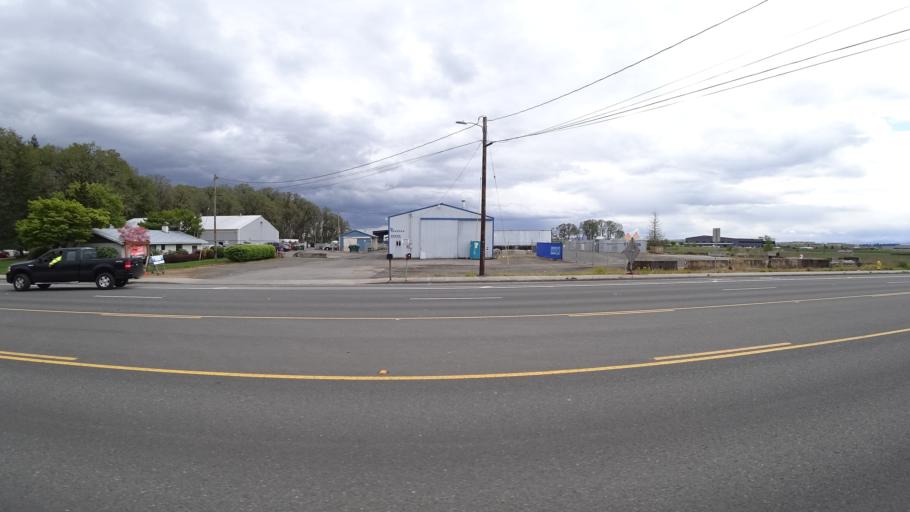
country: US
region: Oregon
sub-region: Washington County
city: Hillsboro
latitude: 45.5511
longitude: -122.9449
